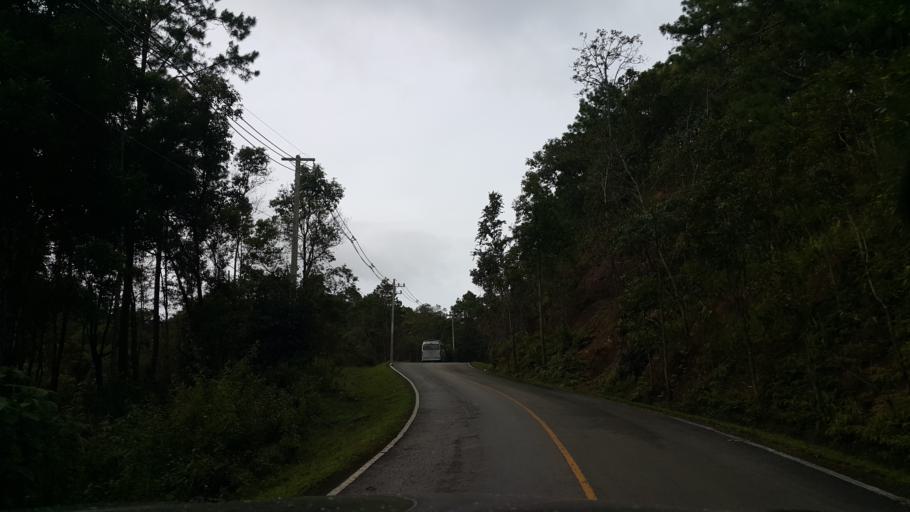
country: TH
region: Chiang Mai
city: Chaem Luang
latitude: 18.9155
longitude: 98.4812
